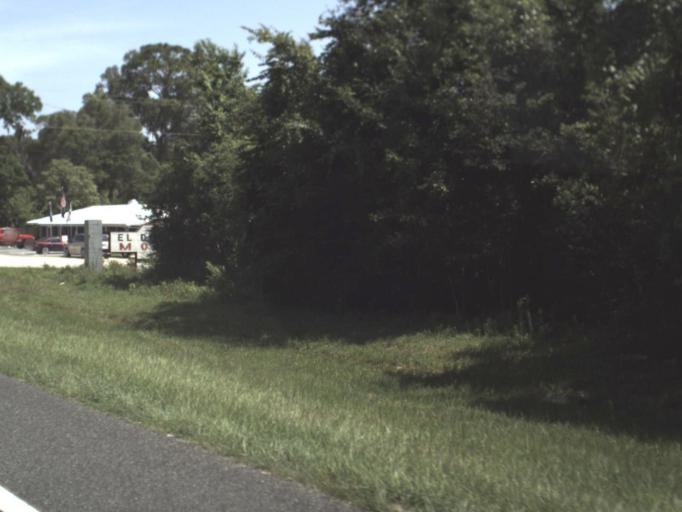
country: US
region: Florida
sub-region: Levy County
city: Manatee Road
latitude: 29.5809
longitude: -82.9187
